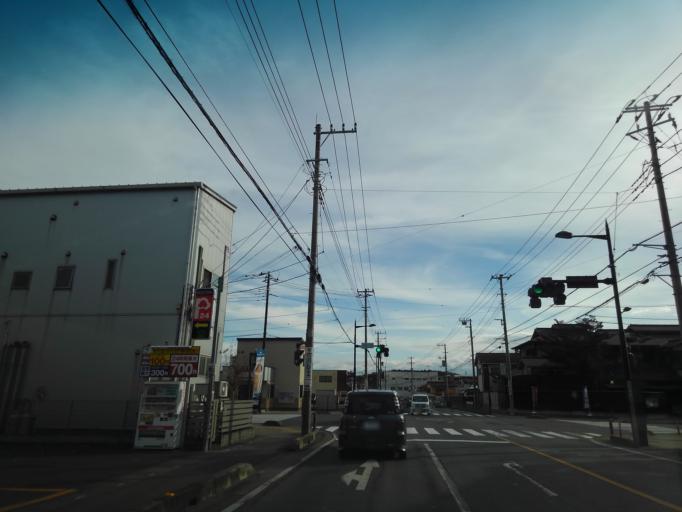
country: JP
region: Saitama
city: Hanno
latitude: 35.8961
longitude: 139.3365
